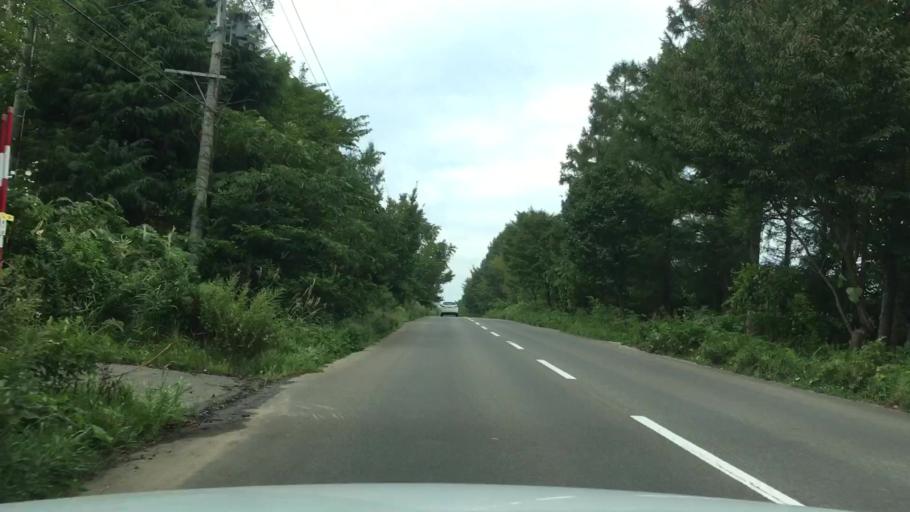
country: JP
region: Aomori
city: Shimokizukuri
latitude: 40.7119
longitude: 140.3284
